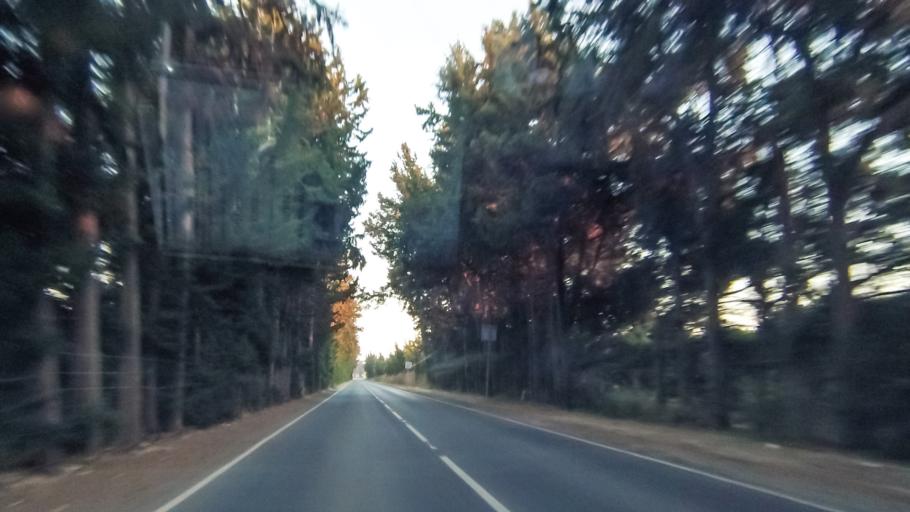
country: CY
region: Larnaka
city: Kolossi
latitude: 34.6487
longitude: 32.9429
